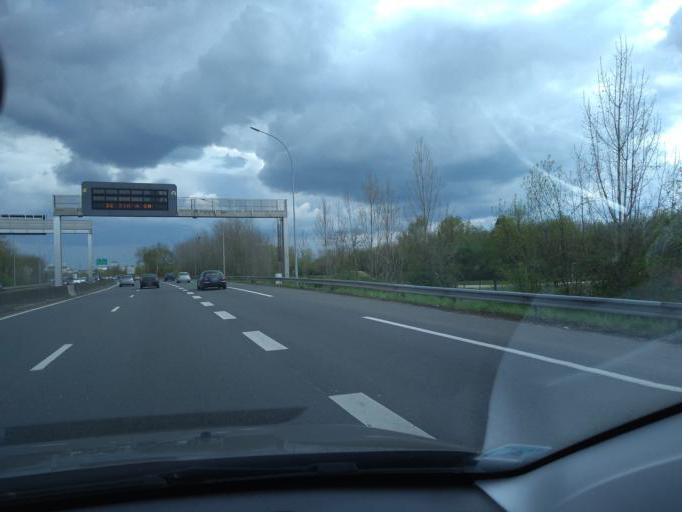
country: FR
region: Pays de la Loire
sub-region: Departement de Maine-et-Loire
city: Angers
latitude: 47.4646
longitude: -0.5738
